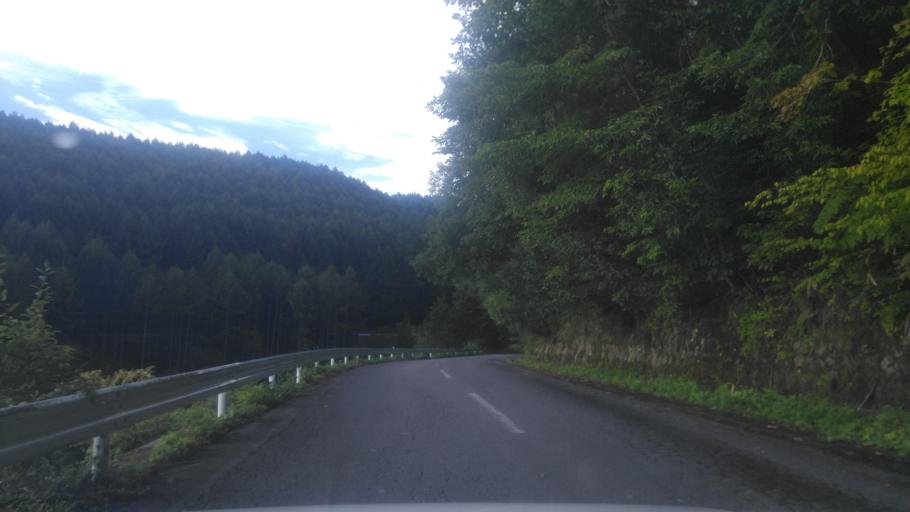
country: JP
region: Nagano
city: Ueda
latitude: 36.5140
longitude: 138.3658
